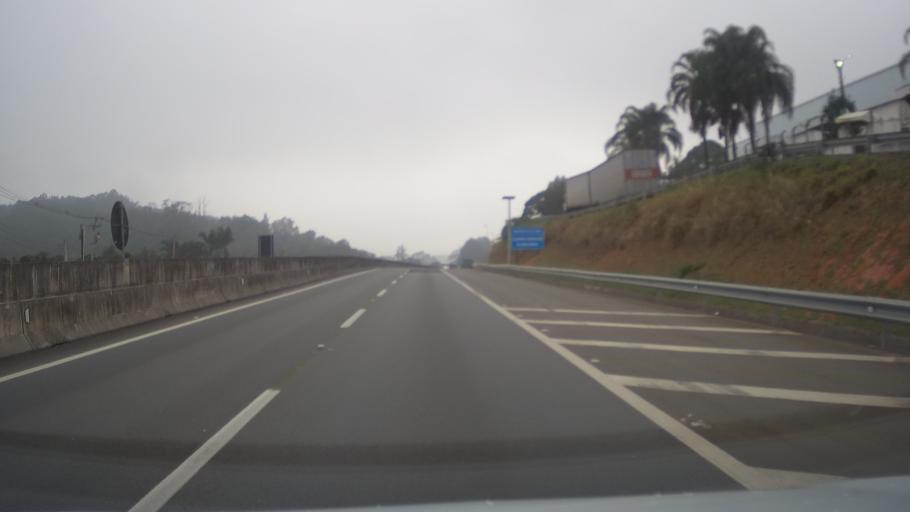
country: BR
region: Sao Paulo
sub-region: Itatiba
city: Itatiba
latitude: -23.0813
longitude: -46.8446
